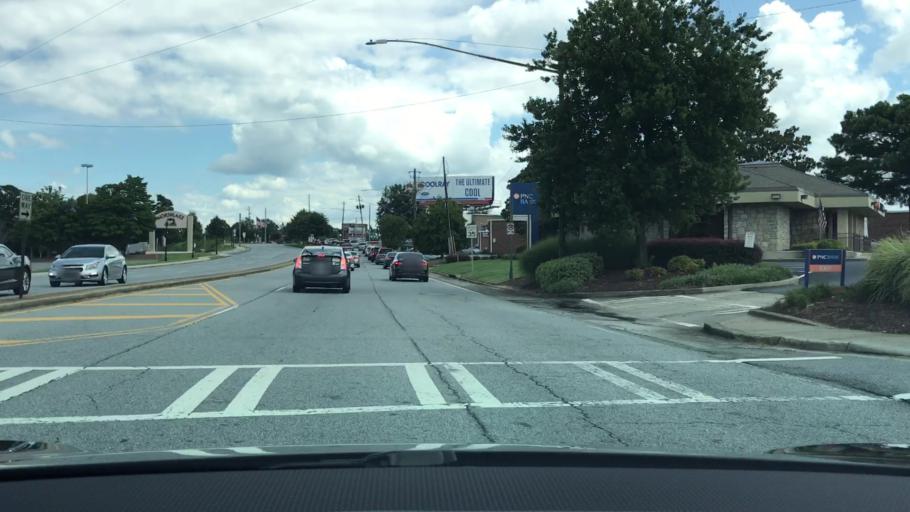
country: US
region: Georgia
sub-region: DeKalb County
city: Tucker
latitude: 33.8480
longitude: -84.2556
